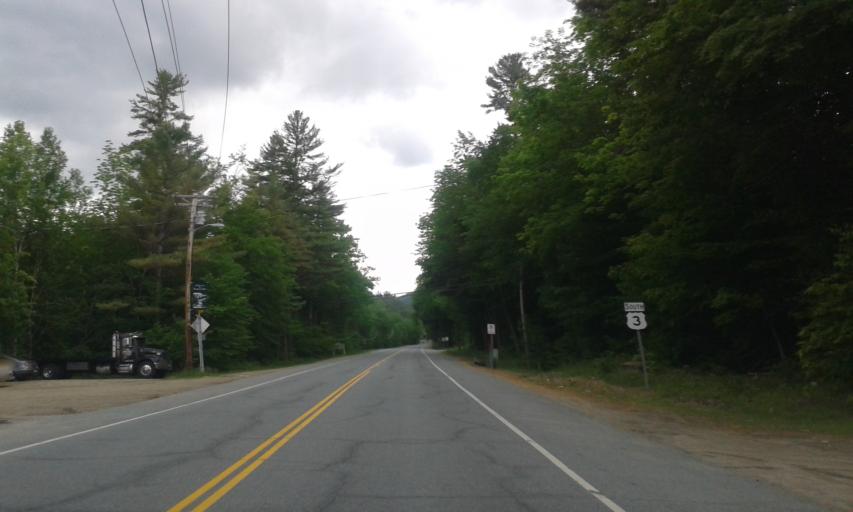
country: US
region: New Hampshire
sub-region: Grafton County
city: Woodstock
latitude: 44.0469
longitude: -71.6863
